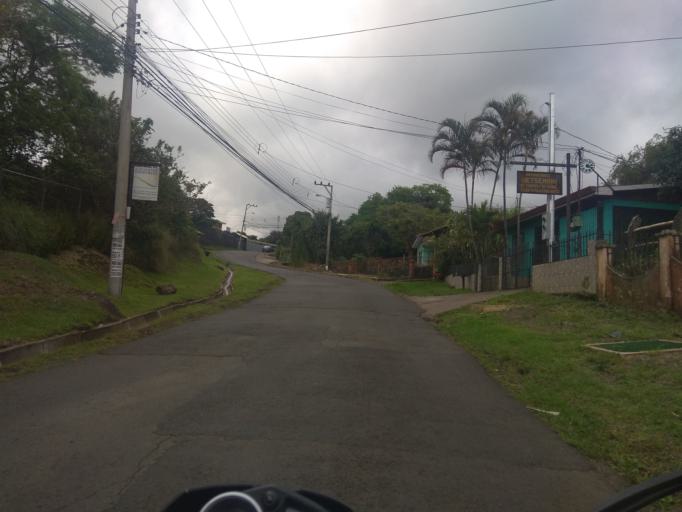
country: CR
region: Heredia
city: San Josecito
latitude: 10.0263
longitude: -84.1076
